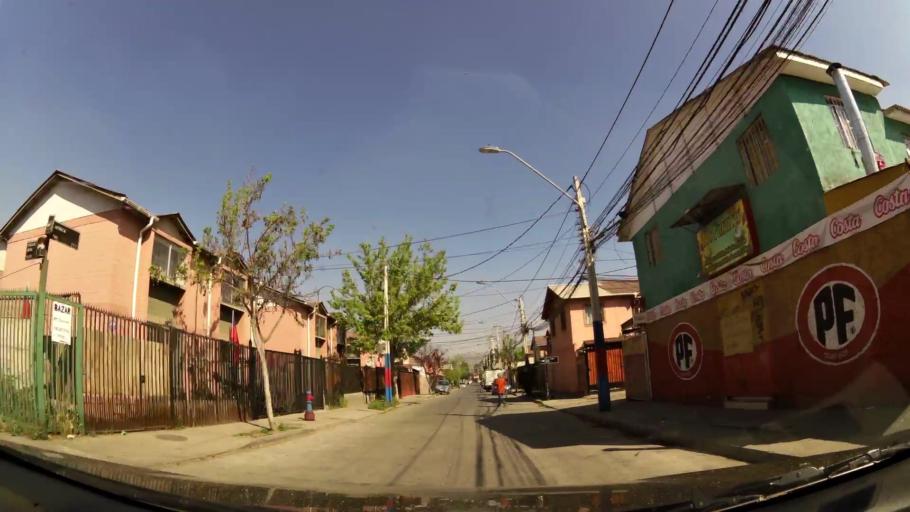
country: CL
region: Santiago Metropolitan
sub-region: Provincia de Santiago
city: Lo Prado
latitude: -33.3560
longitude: -70.7413
